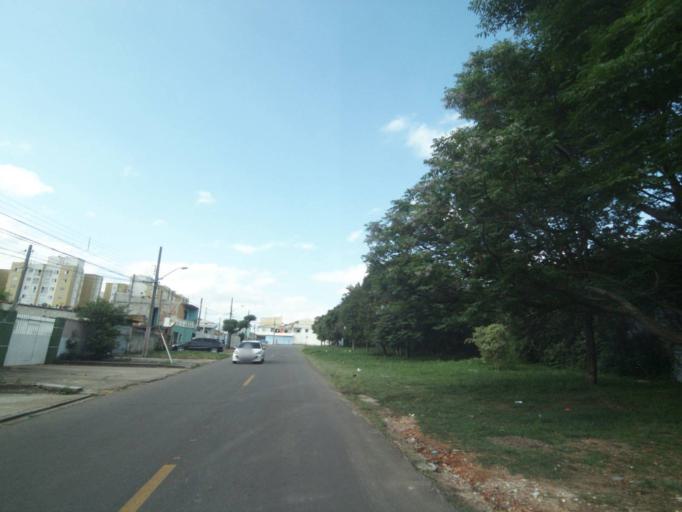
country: BR
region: Parana
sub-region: Curitiba
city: Curitiba
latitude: -25.4987
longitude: -49.3246
